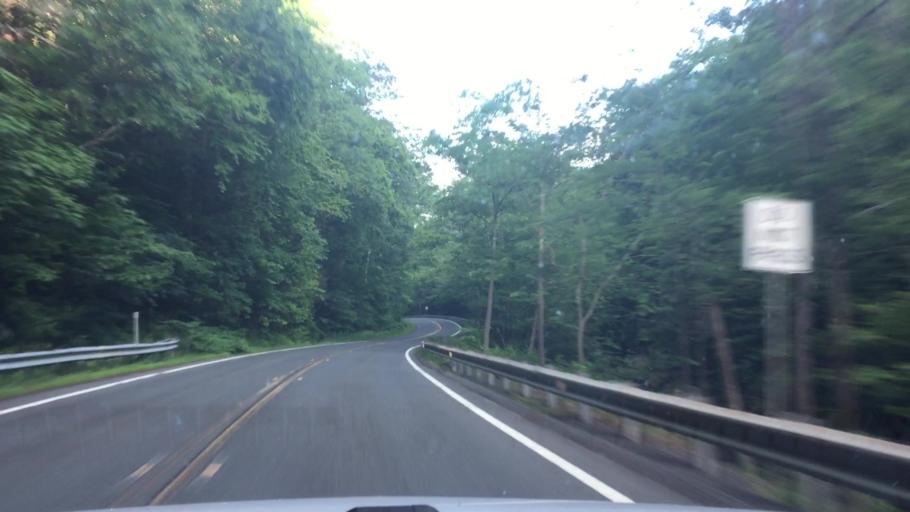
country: US
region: Massachusetts
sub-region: Hampshire County
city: Chesterfield
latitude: 42.3287
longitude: -72.8752
